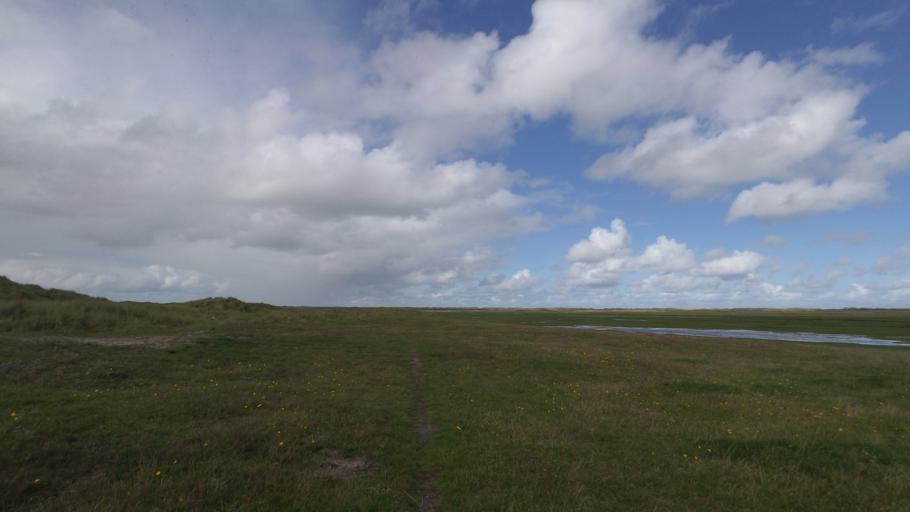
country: NL
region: Friesland
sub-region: Gemeente Ameland
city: Nes
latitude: 53.4485
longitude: 5.8626
